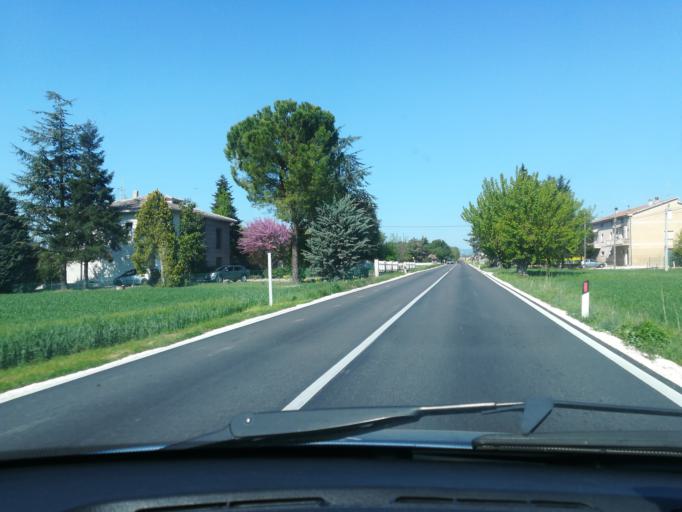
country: IT
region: The Marches
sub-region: Provincia di Macerata
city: Villa Potenza
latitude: 43.3255
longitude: 13.4071
